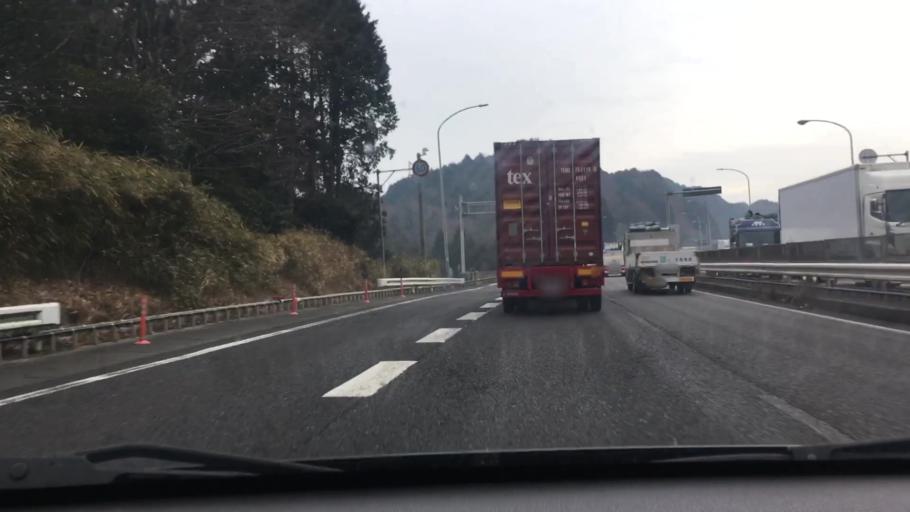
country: JP
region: Mie
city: Ueno-ebisumachi
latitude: 34.8391
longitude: 136.2675
